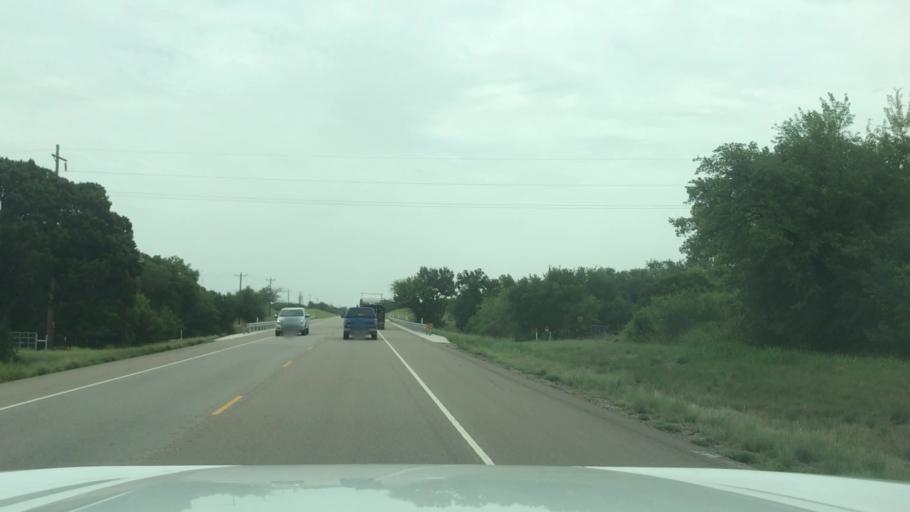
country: US
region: Texas
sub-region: Bosque County
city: Meridian
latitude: 31.9280
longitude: -97.6881
